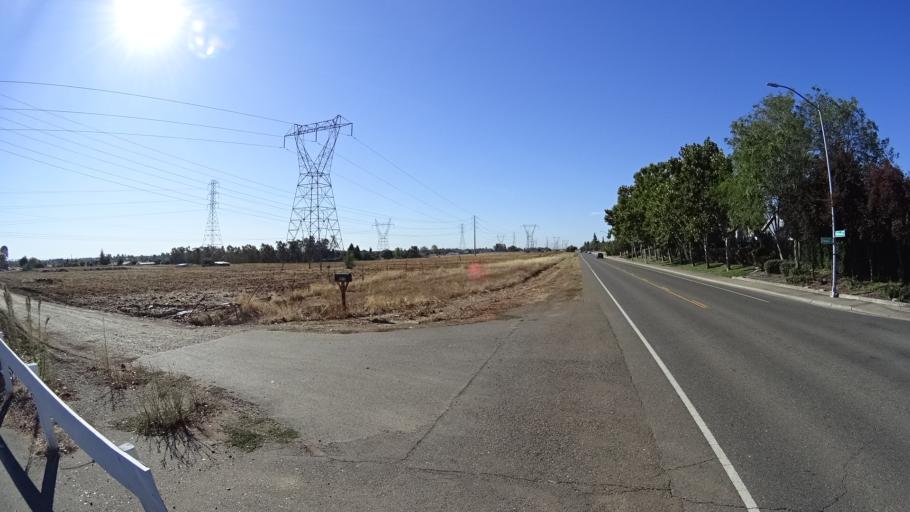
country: US
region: California
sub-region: Sacramento County
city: Vineyard
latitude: 38.4491
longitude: -121.3533
